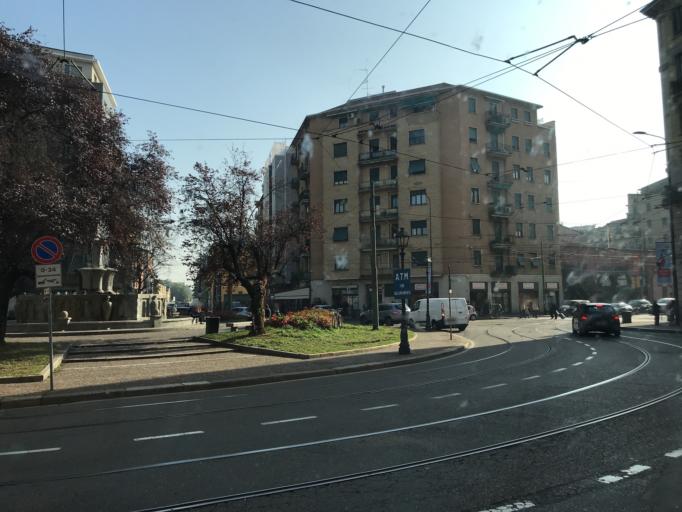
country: IT
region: Lombardy
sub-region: Citta metropolitana di Milano
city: Novate Milanese
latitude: 45.5021
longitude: 9.1650
